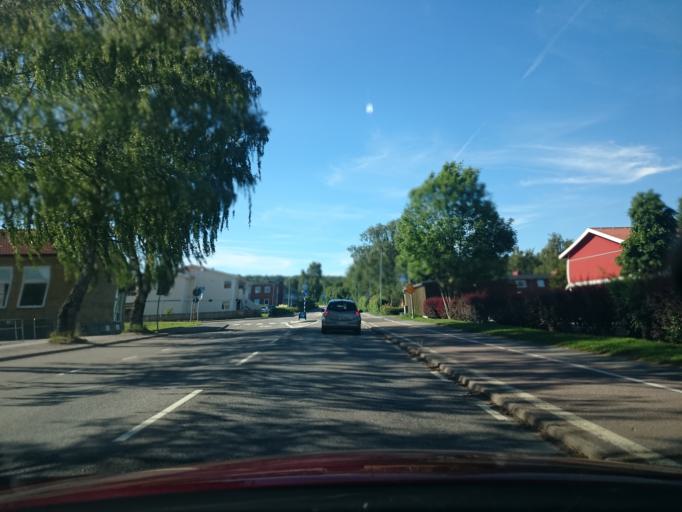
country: SE
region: Vaestra Goetaland
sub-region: Lerums Kommun
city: Lerum
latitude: 57.7726
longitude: 12.2680
